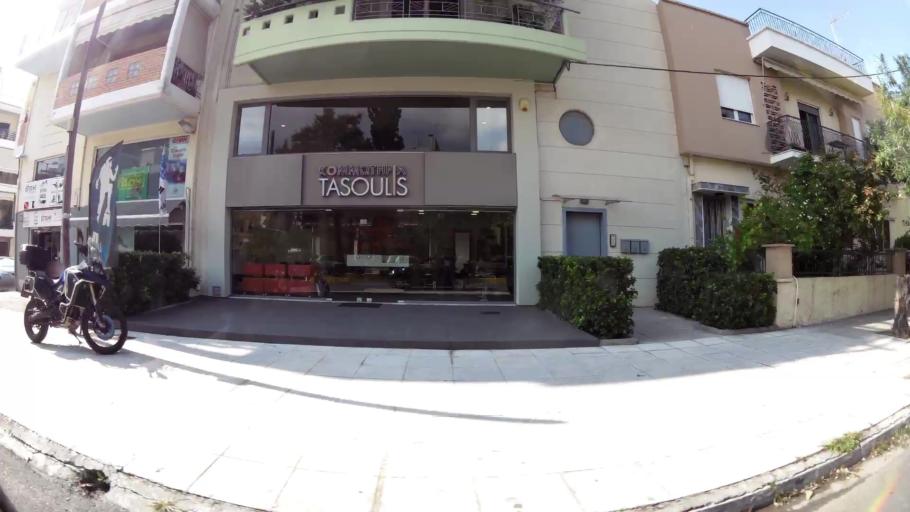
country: GR
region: Attica
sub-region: Nomarchia Athinas
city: Ilioupoli
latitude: 37.9287
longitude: 23.7512
